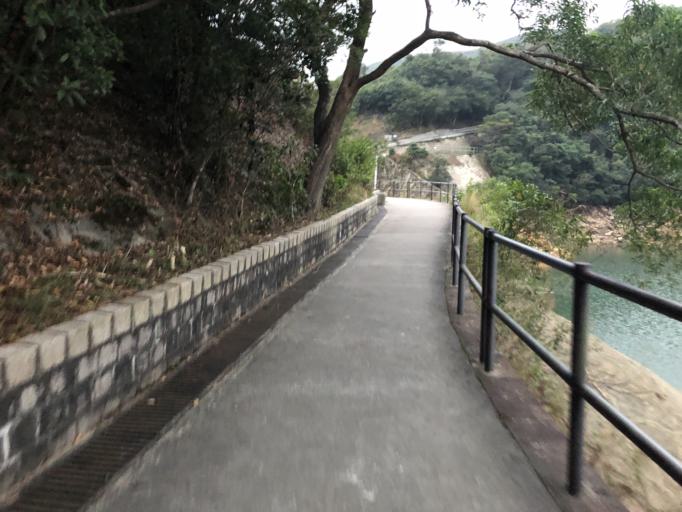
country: HK
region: Wanchai
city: Wan Chai
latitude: 22.2577
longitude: 114.2106
